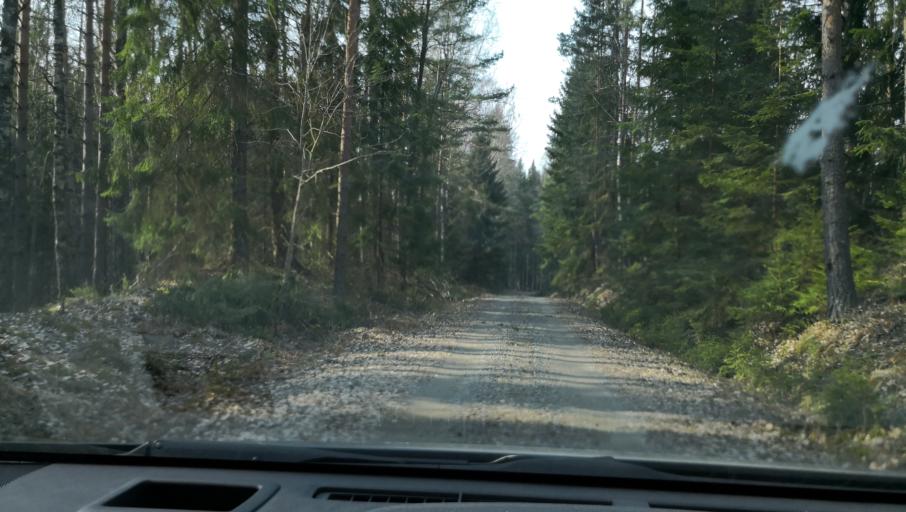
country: SE
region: OErebro
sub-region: Lindesbergs Kommun
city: Frovi
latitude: 59.3854
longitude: 15.4066
